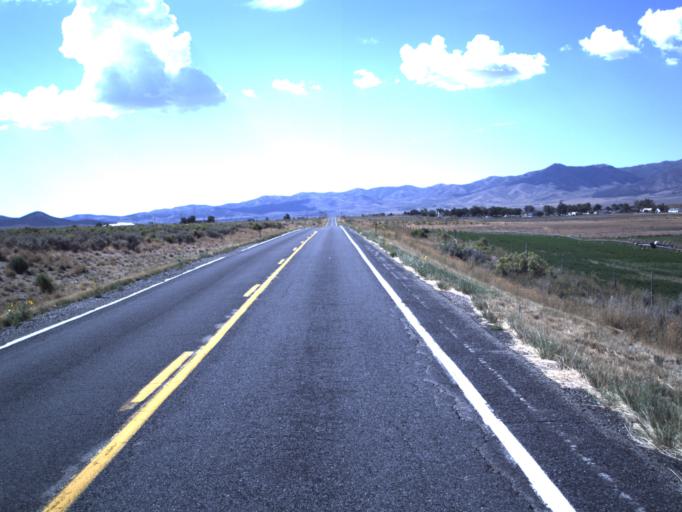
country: US
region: Utah
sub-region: Tooele County
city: Tooele
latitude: 40.1108
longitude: -112.4308
